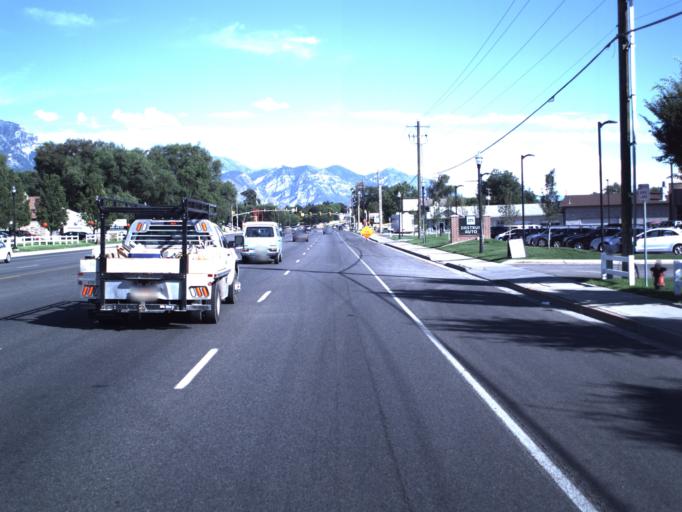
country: US
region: Utah
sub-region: Utah County
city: Lindon
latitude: 40.3466
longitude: -111.7255
